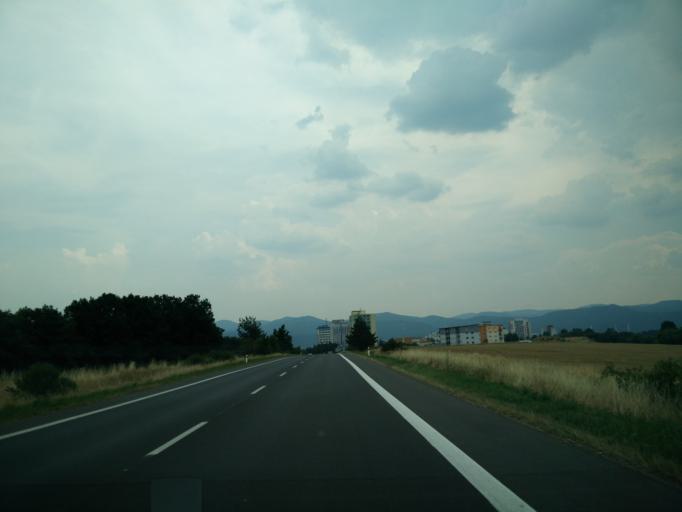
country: SK
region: Banskobystricky
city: Ziar nad Hronom
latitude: 48.6052
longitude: 18.8377
